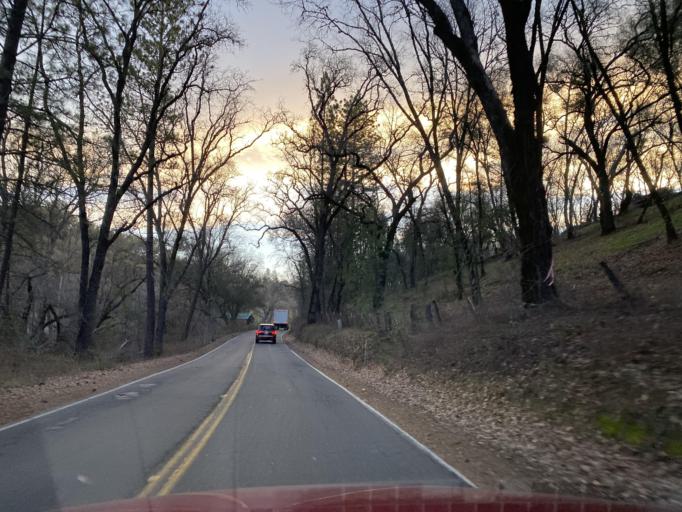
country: US
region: California
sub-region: Amador County
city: Plymouth
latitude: 38.5082
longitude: -120.7733
